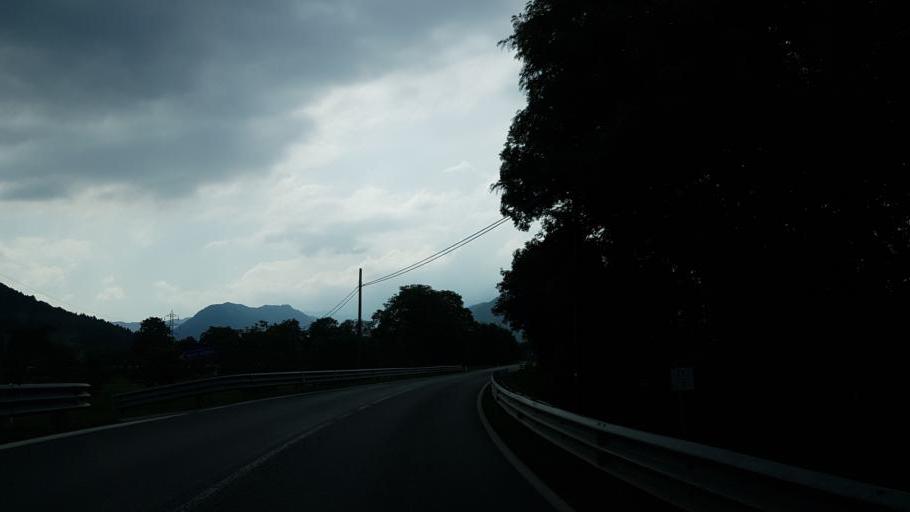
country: IT
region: Piedmont
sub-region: Provincia di Cuneo
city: Roccasparvera
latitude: 44.3333
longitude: 7.4408
